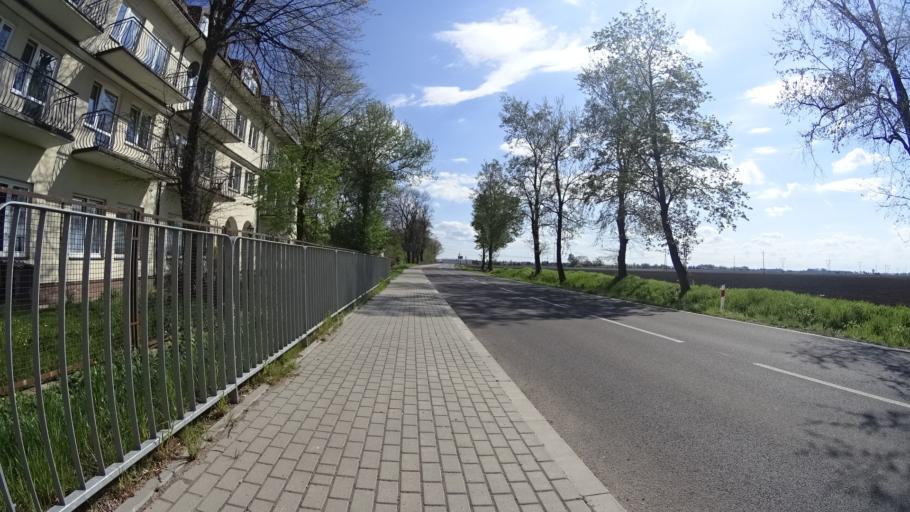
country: PL
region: Masovian Voivodeship
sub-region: Powiat warszawski zachodni
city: Jozefow
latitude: 52.2318
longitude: 20.6930
